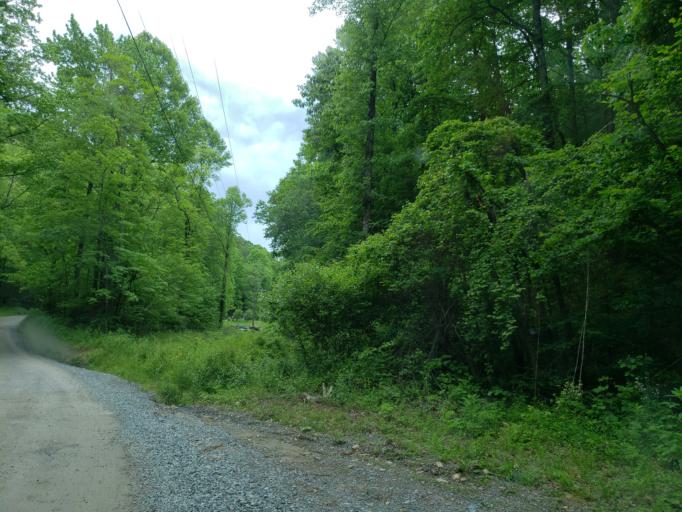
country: US
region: Georgia
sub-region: Fannin County
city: Blue Ridge
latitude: 34.8420
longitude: -84.4150
